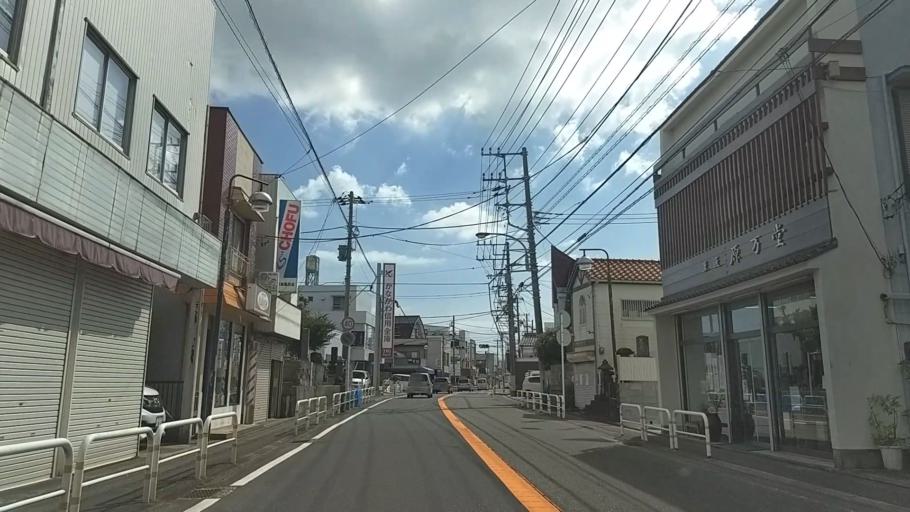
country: JP
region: Kanagawa
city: Miura
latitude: 35.1489
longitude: 139.6273
